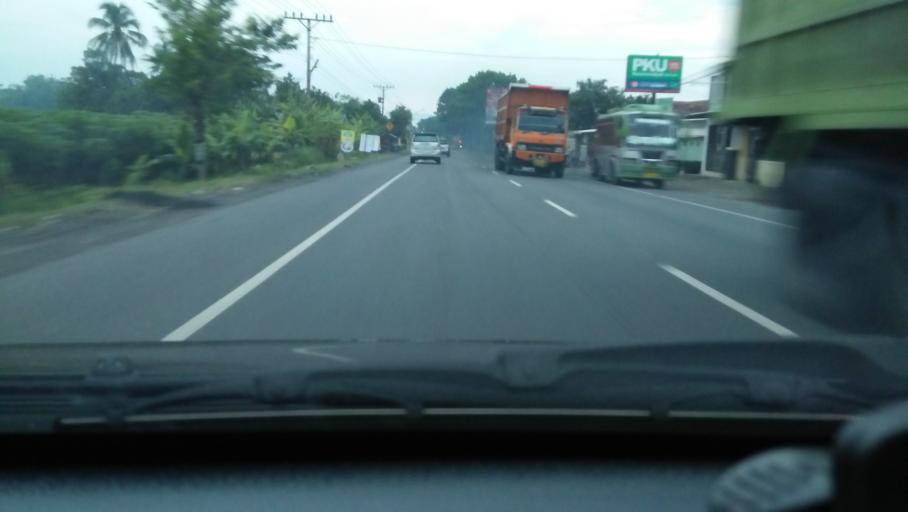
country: ID
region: Central Java
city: Magelang
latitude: -7.4042
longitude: 110.2399
